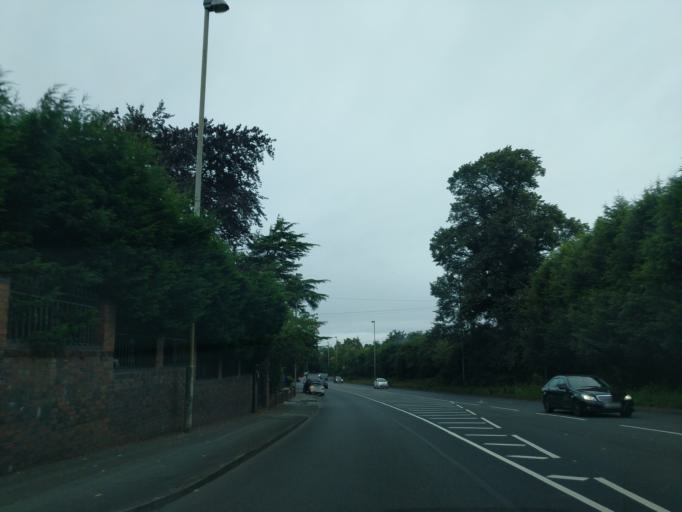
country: GB
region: England
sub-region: Worcestershire
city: Hagley
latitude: 52.4325
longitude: -2.1301
